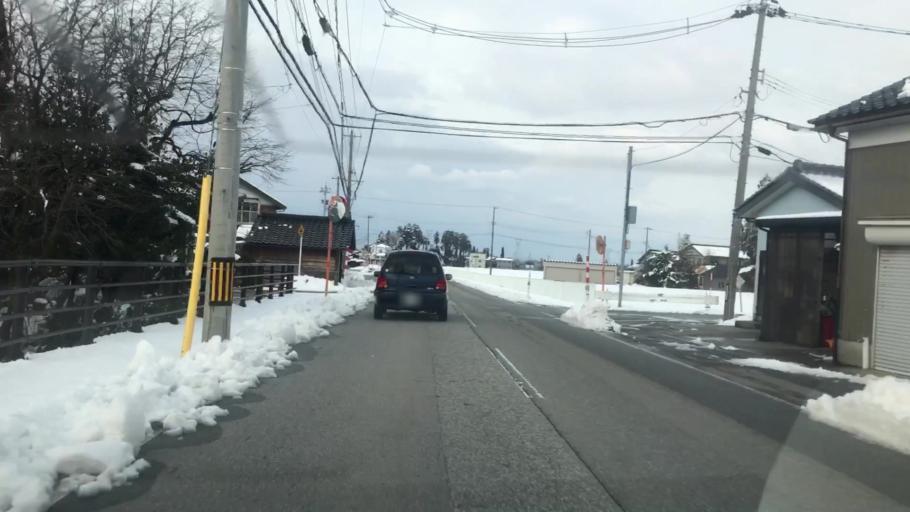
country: JP
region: Toyama
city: Toyama-shi
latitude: 36.6742
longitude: 137.2897
